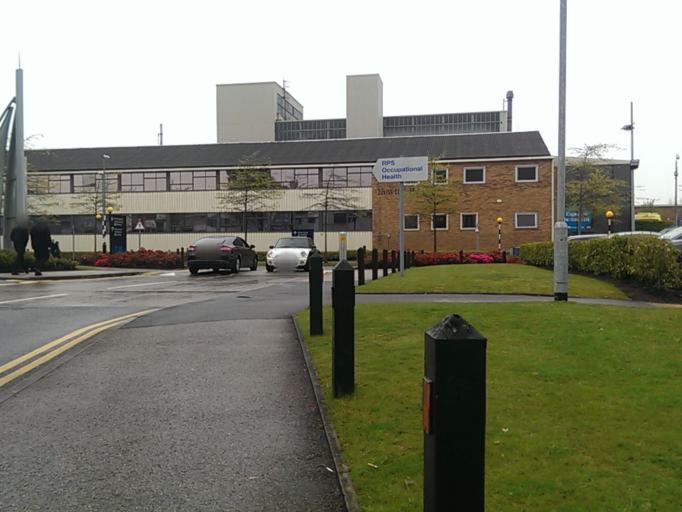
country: GB
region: England
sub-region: Warrington
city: Culcheth
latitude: 53.4269
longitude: -2.5242
